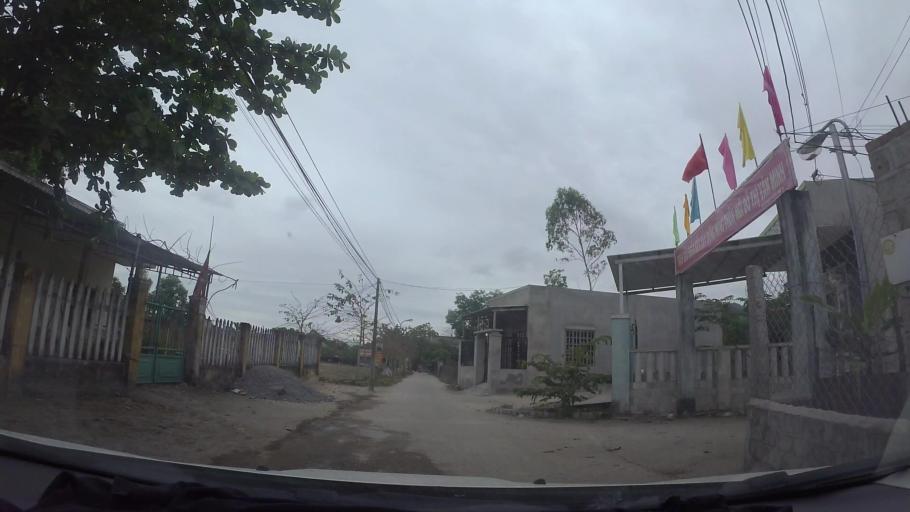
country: VN
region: Da Nang
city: Lien Chieu
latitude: 16.0766
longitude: 108.0978
